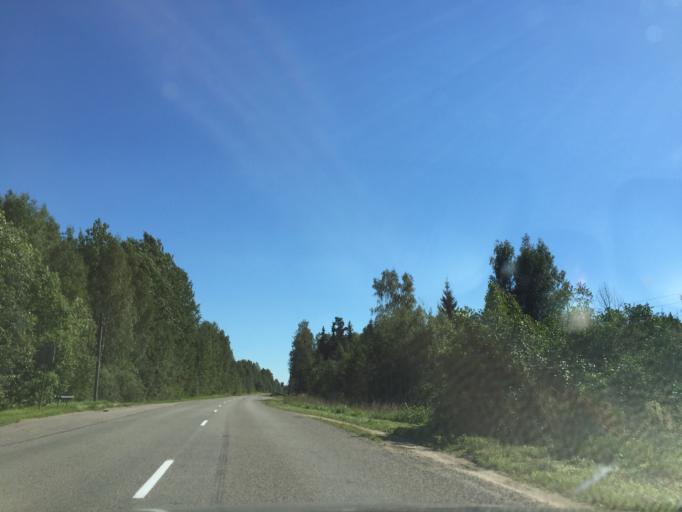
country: LV
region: Akniste
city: Akniste
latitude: 56.0868
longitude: 25.8737
